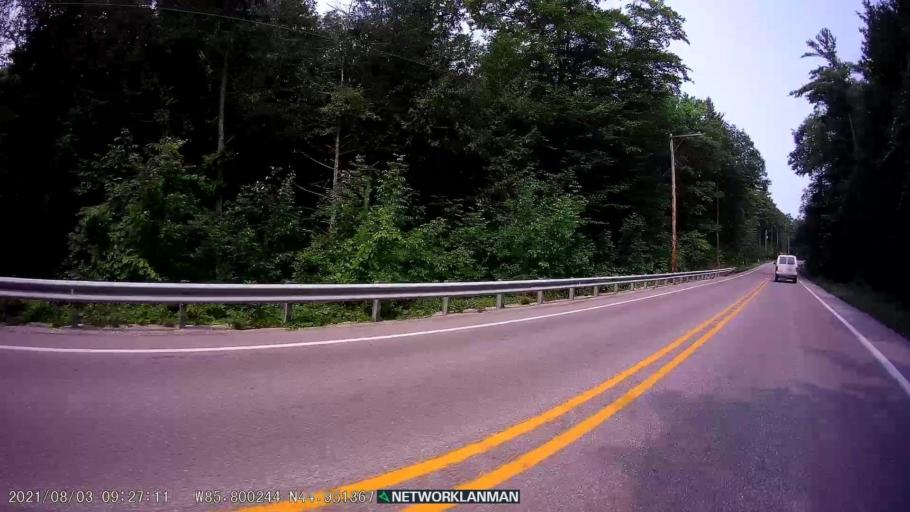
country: US
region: Michigan
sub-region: Leelanau County
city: Leland
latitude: 44.9517
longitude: -85.8003
